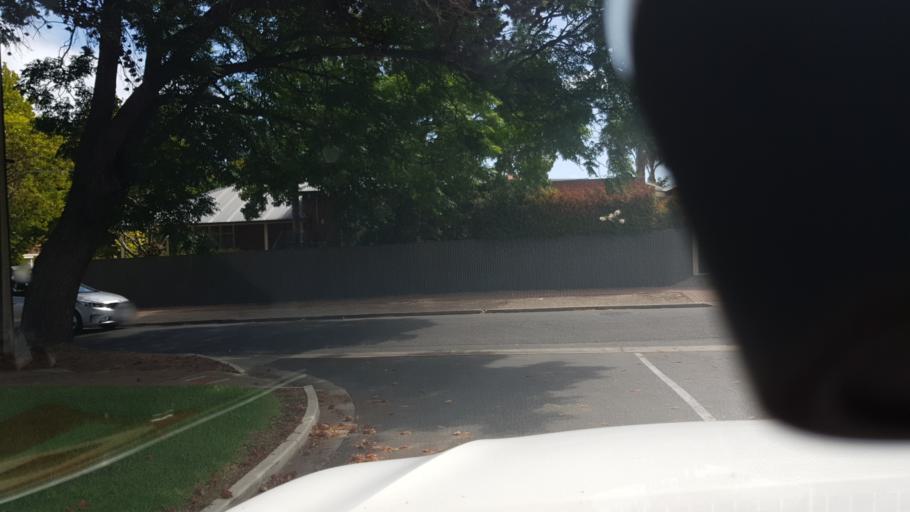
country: AU
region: South Australia
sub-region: Holdfast Bay
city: Glenelg East
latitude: -34.9776
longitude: 138.5244
